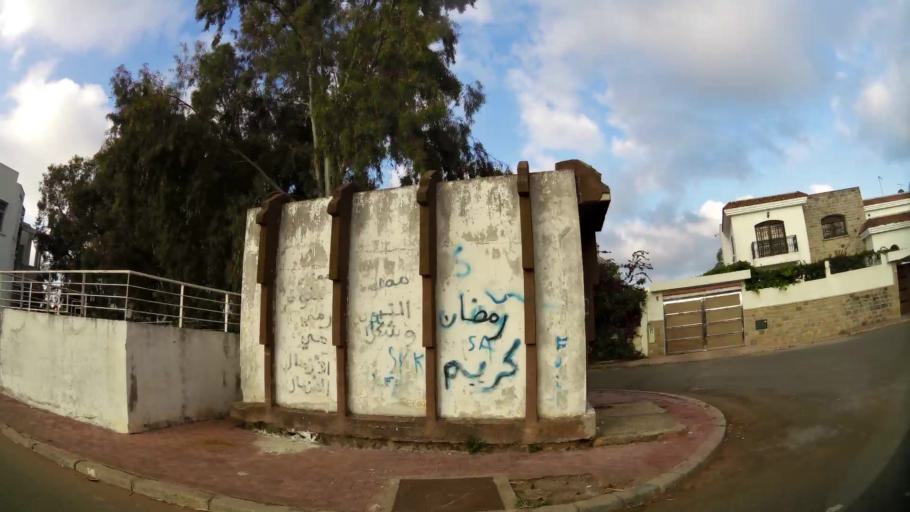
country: MA
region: Rabat-Sale-Zemmour-Zaer
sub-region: Rabat
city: Rabat
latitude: 33.9617
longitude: -6.8511
